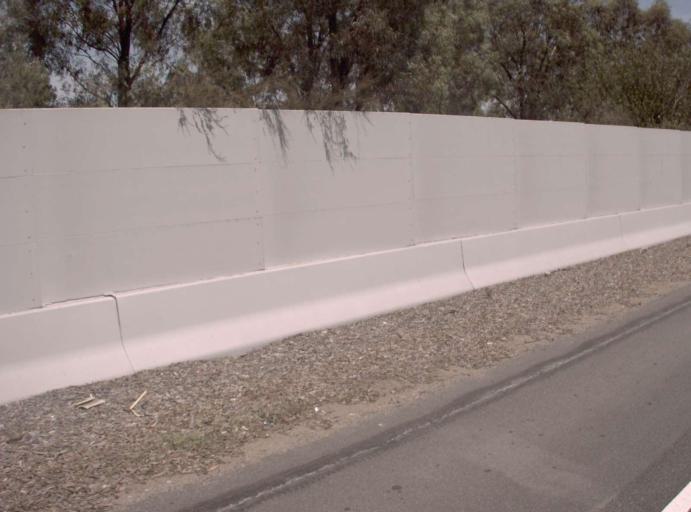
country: AU
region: Victoria
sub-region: Monash
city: Chadstone
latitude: -37.8838
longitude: 145.0921
